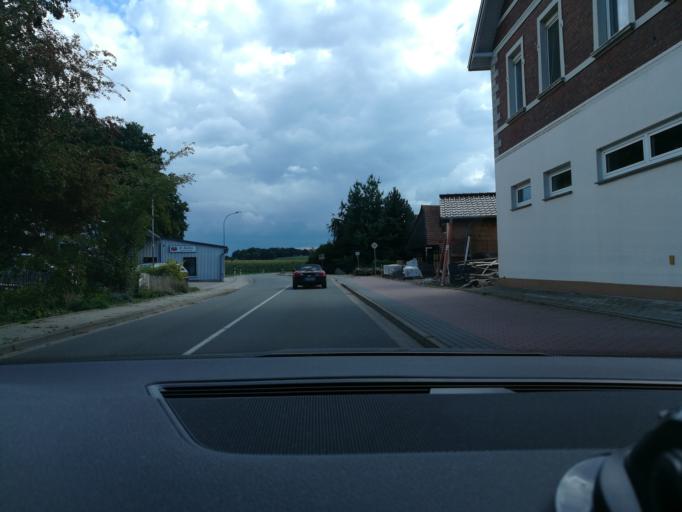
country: DE
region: North Rhine-Westphalia
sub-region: Regierungsbezirk Detmold
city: Minden
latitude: 52.3345
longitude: 8.8519
